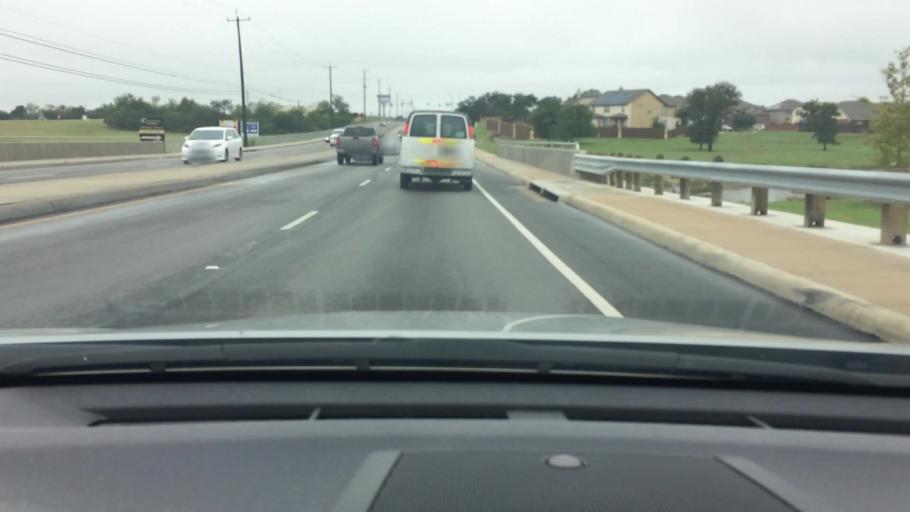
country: US
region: Texas
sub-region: Bexar County
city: Helotes
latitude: 29.5073
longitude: -98.7389
